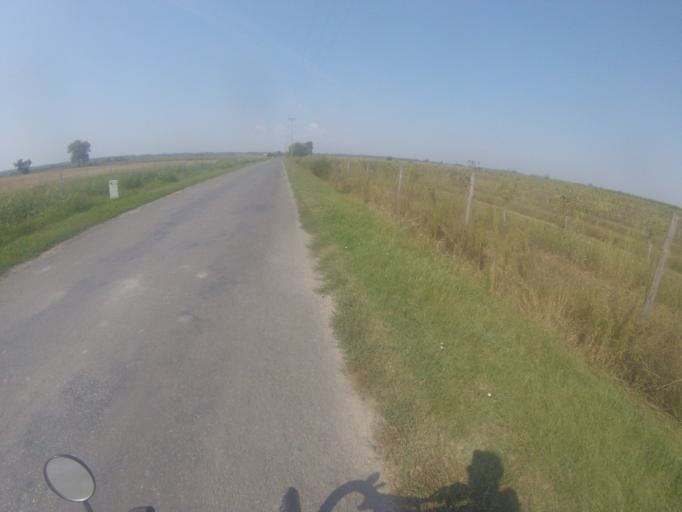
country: HU
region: Bacs-Kiskun
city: Ersekcsanad
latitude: 46.2552
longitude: 18.9534
